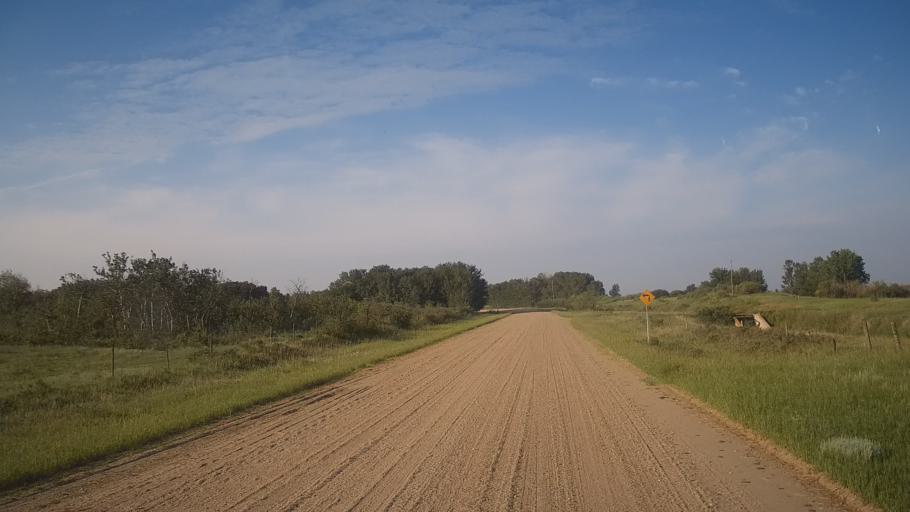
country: CA
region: Saskatchewan
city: Saskatoon
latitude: 51.8268
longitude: -106.5420
